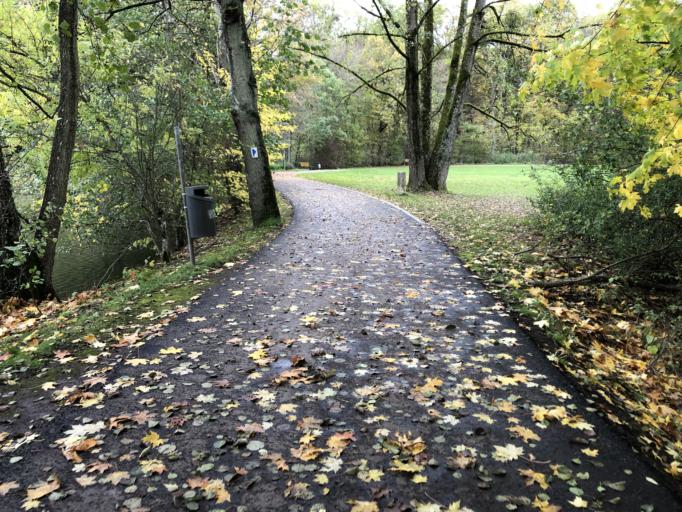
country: LU
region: Luxembourg
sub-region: Canton d'Esch-sur-Alzette
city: Leudelange
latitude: 49.5670
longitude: 6.1057
